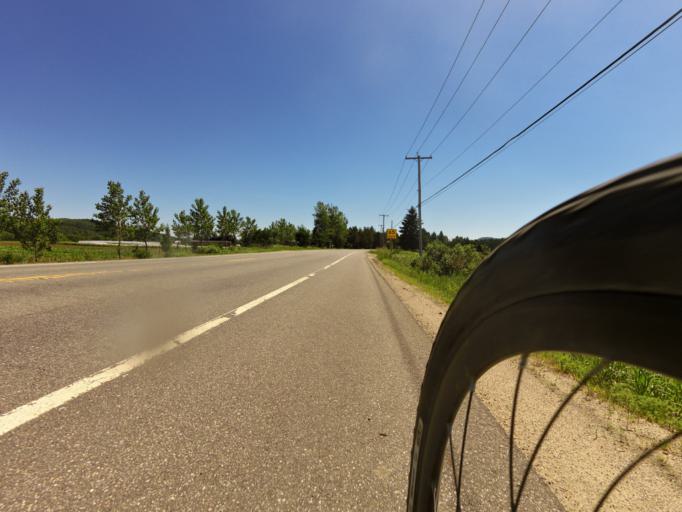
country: CA
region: Quebec
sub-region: Laurentides
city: Mont-Tremblant
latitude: 46.0850
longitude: -74.6316
